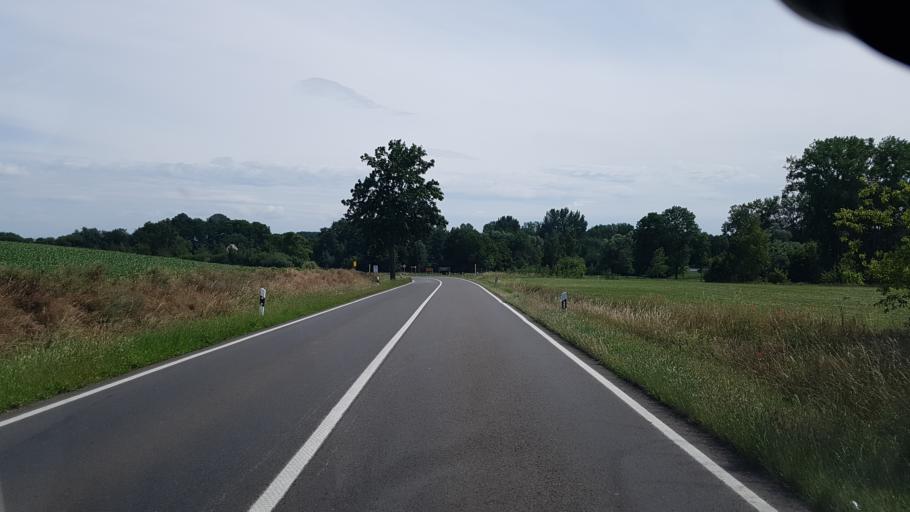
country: DE
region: Brandenburg
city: Prenzlau
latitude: 53.3661
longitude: 13.7924
